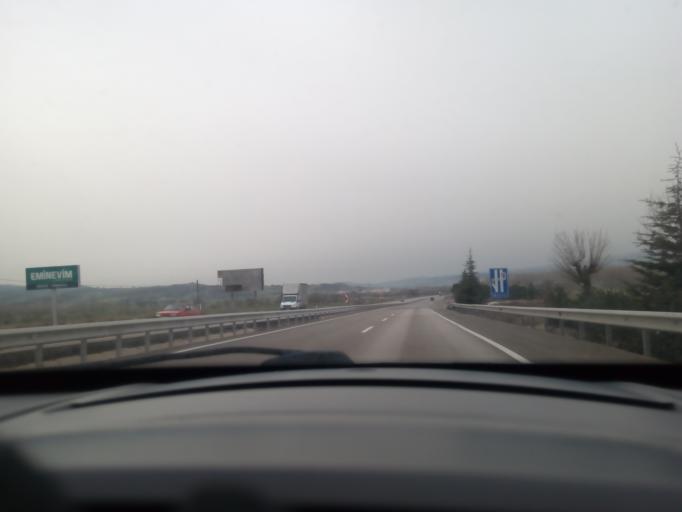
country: TR
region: Balikesir
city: Gobel
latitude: 40.0000
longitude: 28.2191
